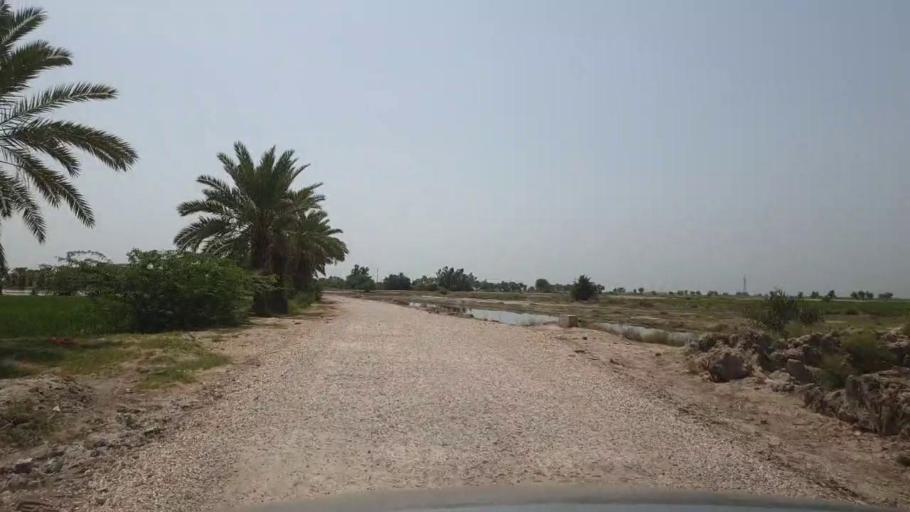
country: PK
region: Sindh
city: Garhi Yasin
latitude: 27.8985
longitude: 68.4937
